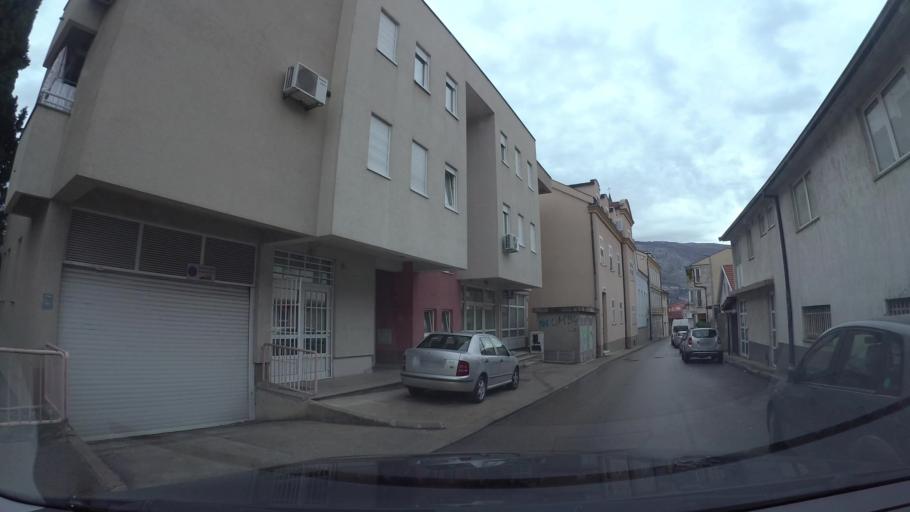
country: BA
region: Federation of Bosnia and Herzegovina
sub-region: Hercegovacko-Bosanski Kanton
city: Mostar
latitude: 43.3377
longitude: 17.8033
